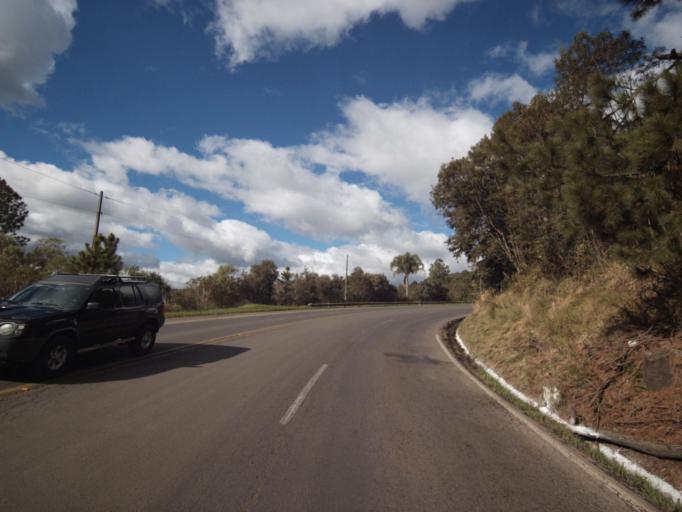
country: BR
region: Santa Catarina
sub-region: Joacaba
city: Joacaba
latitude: -27.0597
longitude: -51.6772
